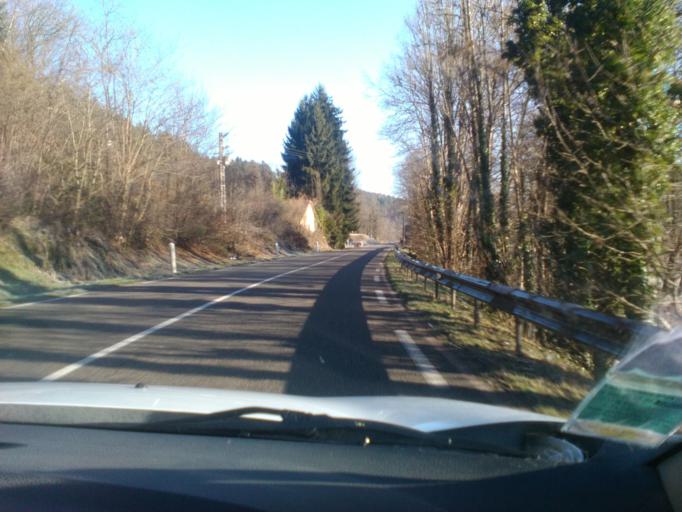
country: FR
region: Alsace
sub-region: Departement du Bas-Rhin
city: Rothau
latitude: 48.4347
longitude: 7.1821
